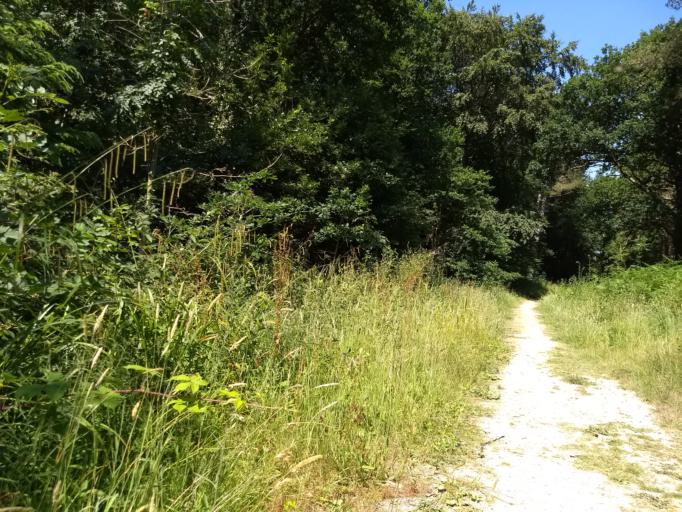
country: GB
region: England
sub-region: Isle of Wight
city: Northwood
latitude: 50.7067
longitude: -1.3338
